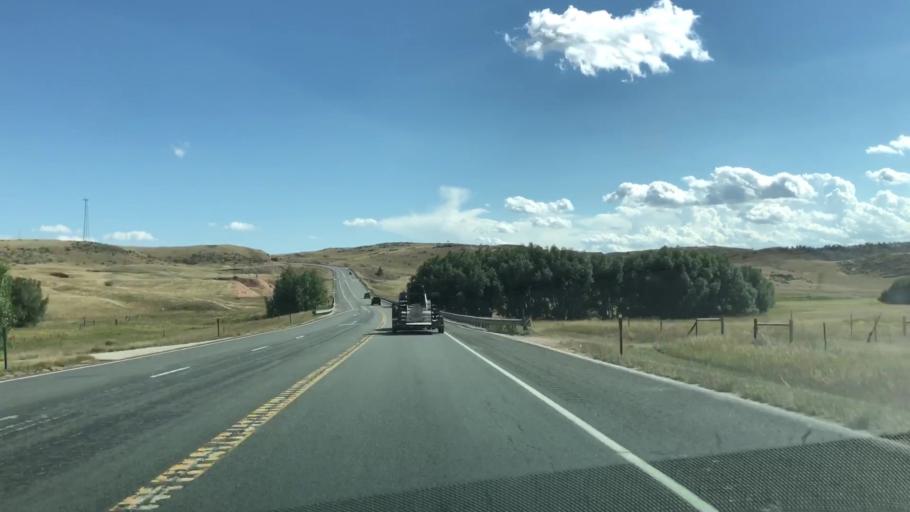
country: US
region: Colorado
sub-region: Larimer County
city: Laporte
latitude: 40.9381
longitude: -105.3425
